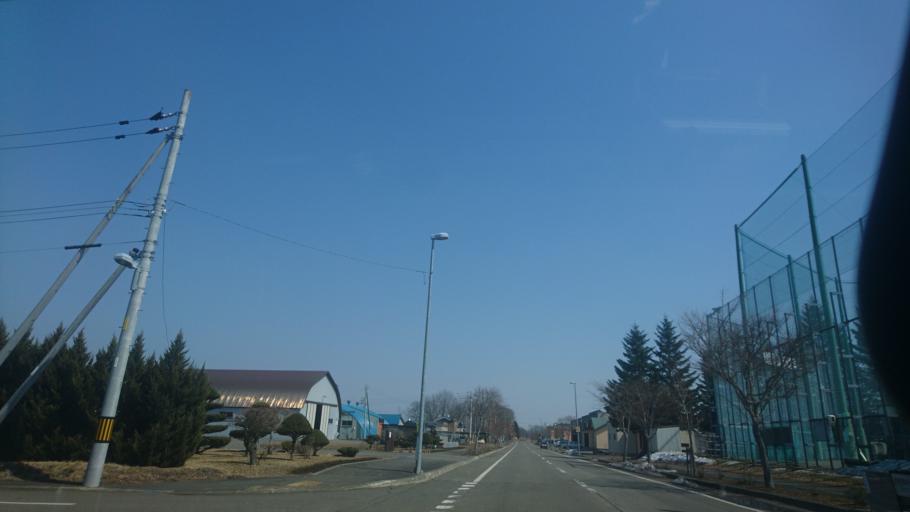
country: JP
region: Hokkaido
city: Obihiro
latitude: 42.9151
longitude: 143.0718
